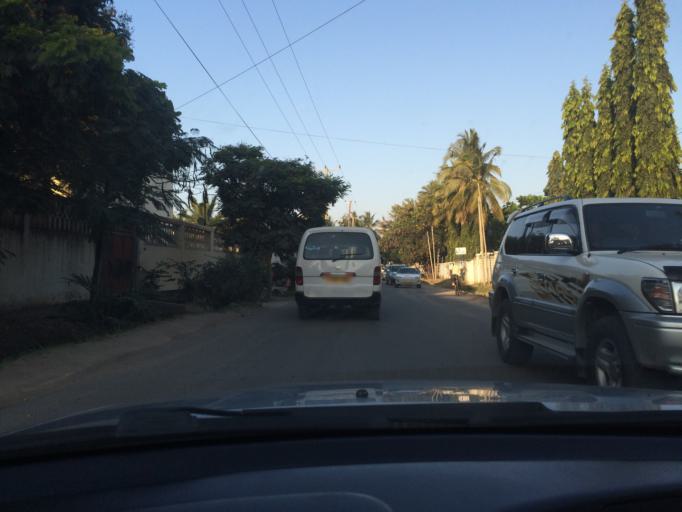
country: TZ
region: Dar es Salaam
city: Magomeni
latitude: -6.7720
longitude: 39.2589
